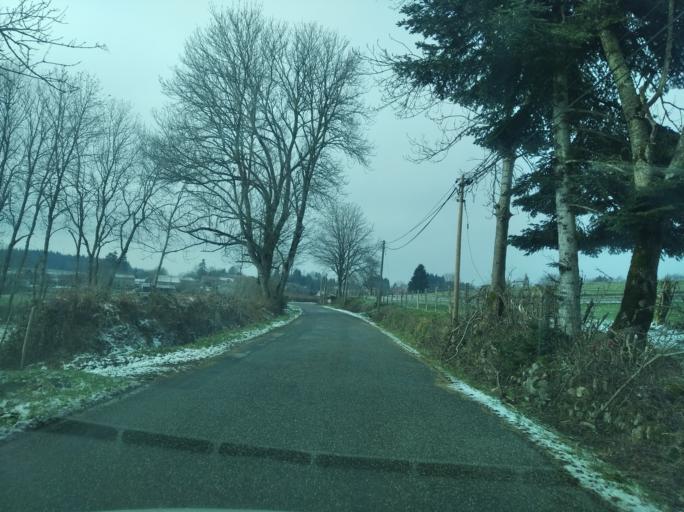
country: FR
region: Rhone-Alpes
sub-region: Departement de la Loire
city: La Pacaudiere
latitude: 46.1146
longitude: 3.8008
